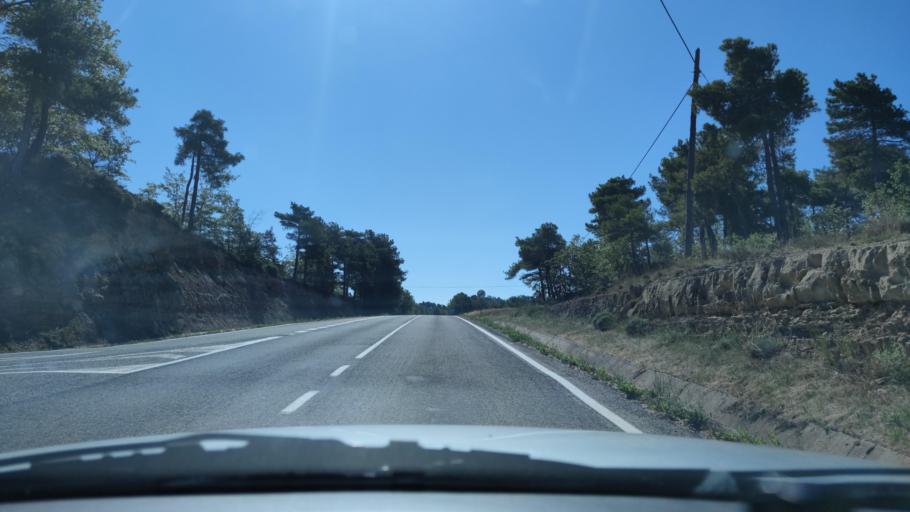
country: ES
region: Catalonia
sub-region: Provincia de Lleida
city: Solsona
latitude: 41.9080
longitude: 1.5297
